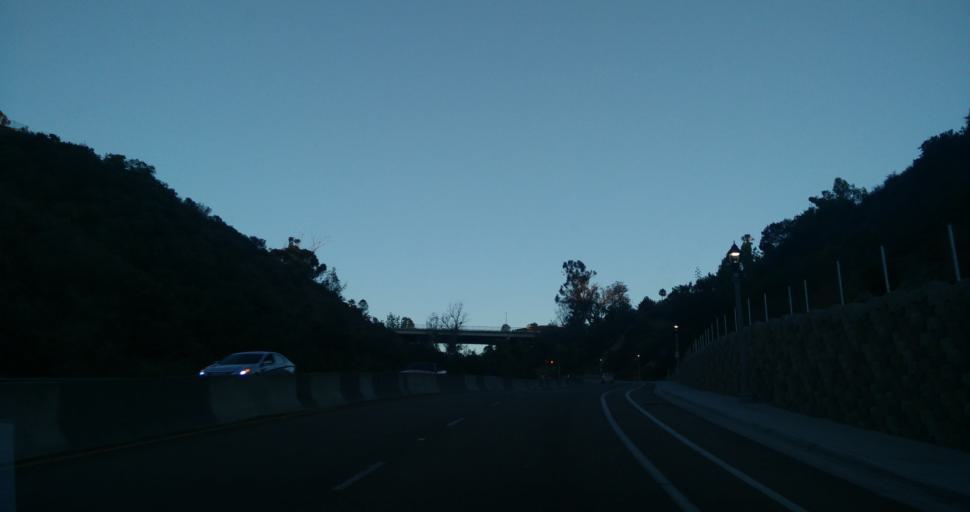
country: US
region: California
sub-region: San Diego County
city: San Diego
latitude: 32.7657
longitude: -117.1390
